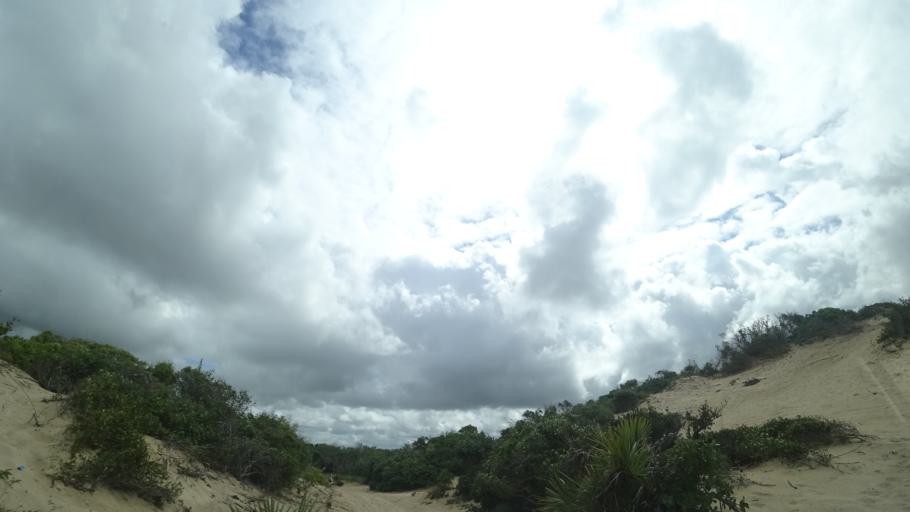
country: MZ
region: Sofala
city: Beira
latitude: -19.6121
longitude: 35.2226
